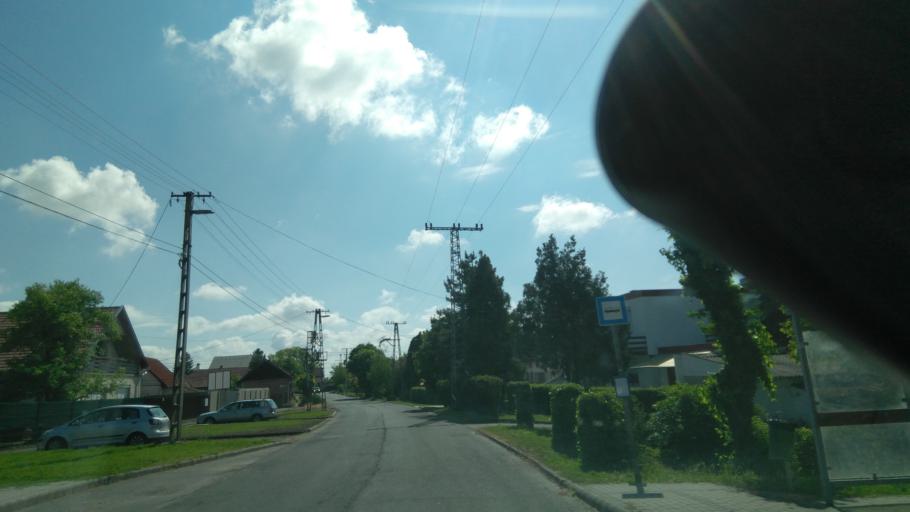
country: HU
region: Bekes
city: Bekes
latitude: 46.7766
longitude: 21.1315
